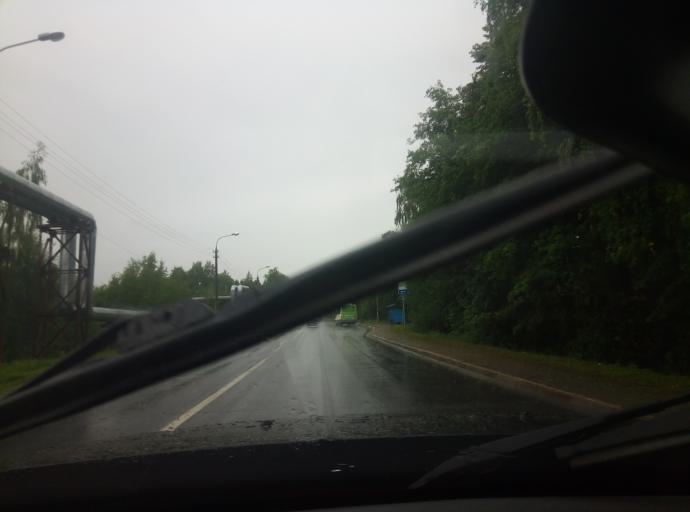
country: RU
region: Moskovskaya
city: Protvino
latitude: 54.8819
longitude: 37.2229
